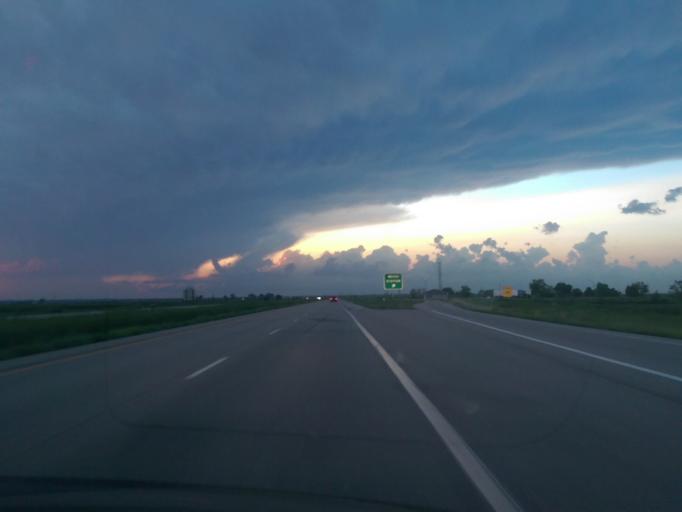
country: US
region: Nebraska
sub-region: Otoe County
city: Nebraska City
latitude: 40.7046
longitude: -95.7939
